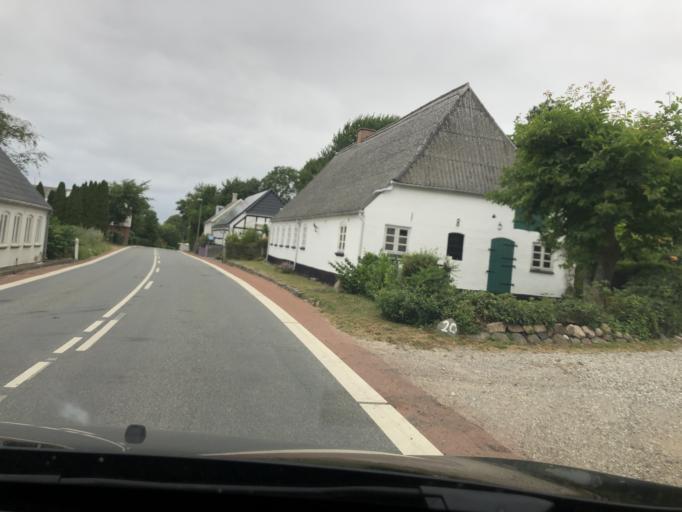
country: DK
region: South Denmark
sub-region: AEro Kommune
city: AEroskobing
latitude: 54.8872
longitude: 10.3221
